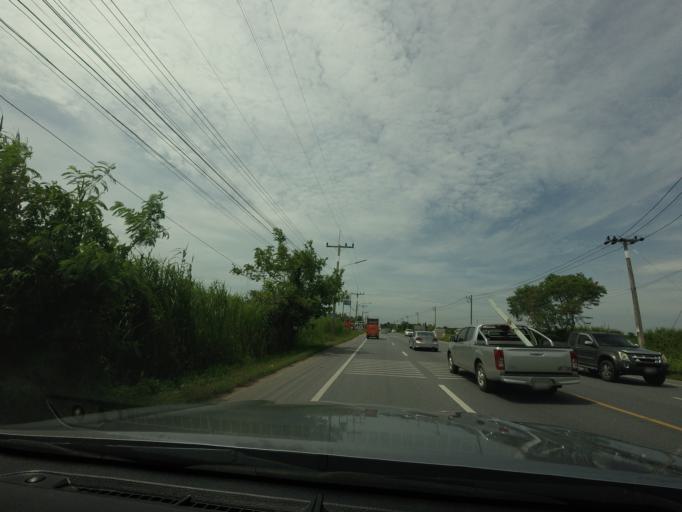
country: TH
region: Nakhon Si Thammarat
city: Nakhon Si Thammarat
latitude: 8.4402
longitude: 99.9831
